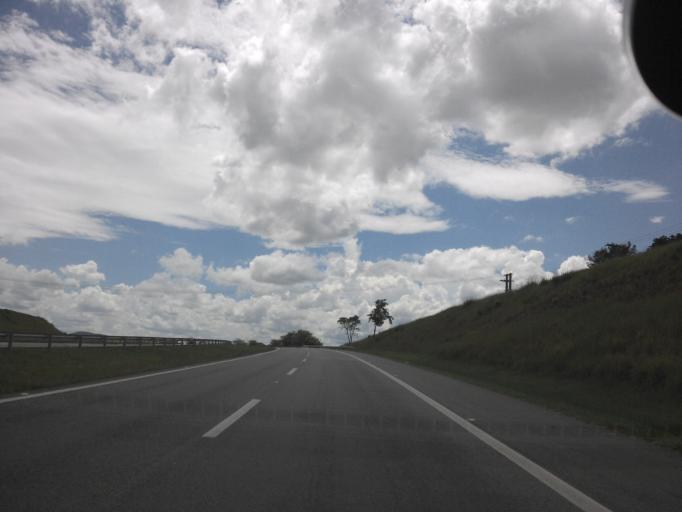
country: BR
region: Sao Paulo
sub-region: Jacarei
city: Jacarei
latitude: -23.3242
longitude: -46.0300
